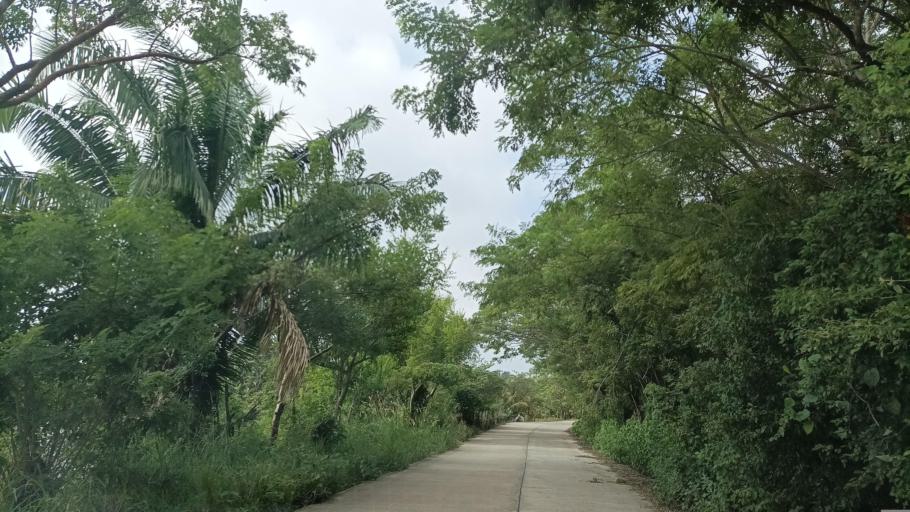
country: MX
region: Veracruz
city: Villa Nanchital
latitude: 18.0938
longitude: -94.2925
